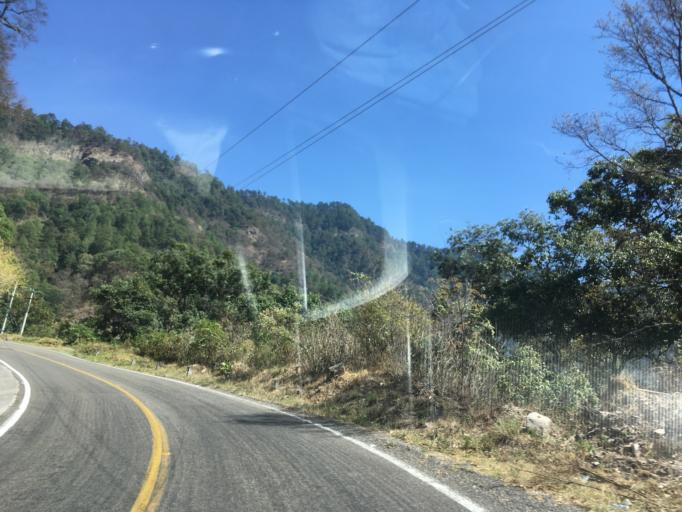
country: MX
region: Michoacan
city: Tzitzio
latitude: 19.6623
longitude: -100.9221
